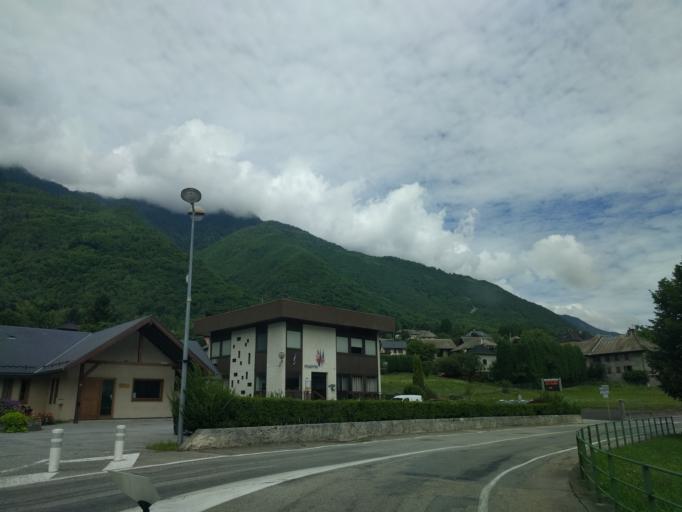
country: FR
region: Rhone-Alpes
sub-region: Departement de la Savoie
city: Saint-Remy-de-Maurienne
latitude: 45.3917
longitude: 6.2658
